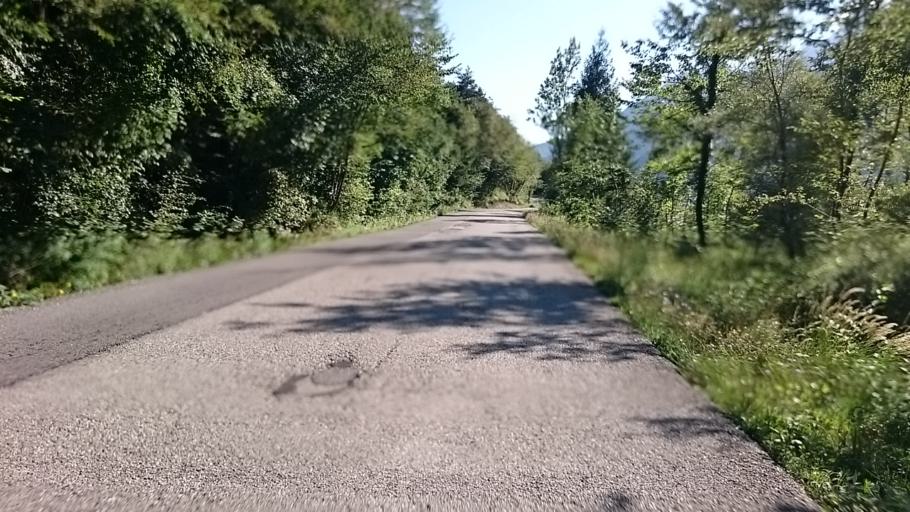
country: IT
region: Veneto
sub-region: Provincia di Belluno
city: Soverzene
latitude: 46.2320
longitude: 12.3038
